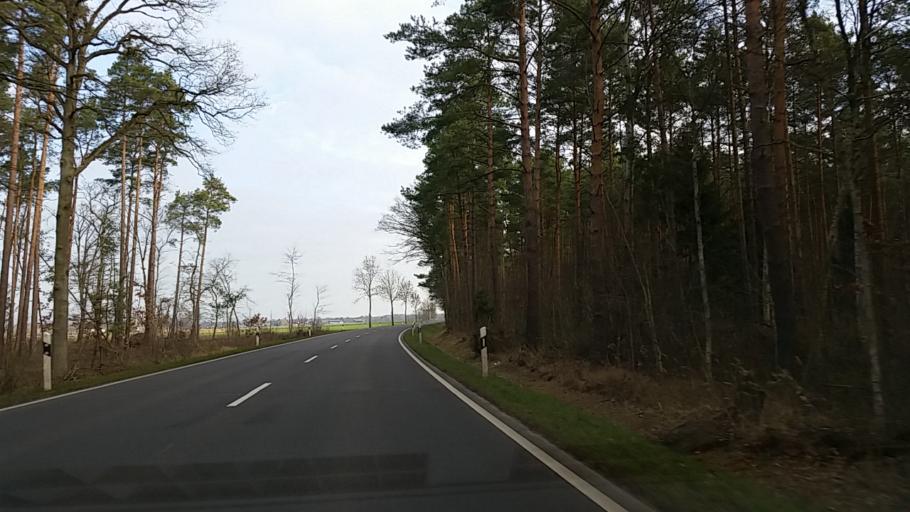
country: DE
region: Lower Saxony
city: Parsau
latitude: 52.5161
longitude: 10.8858
